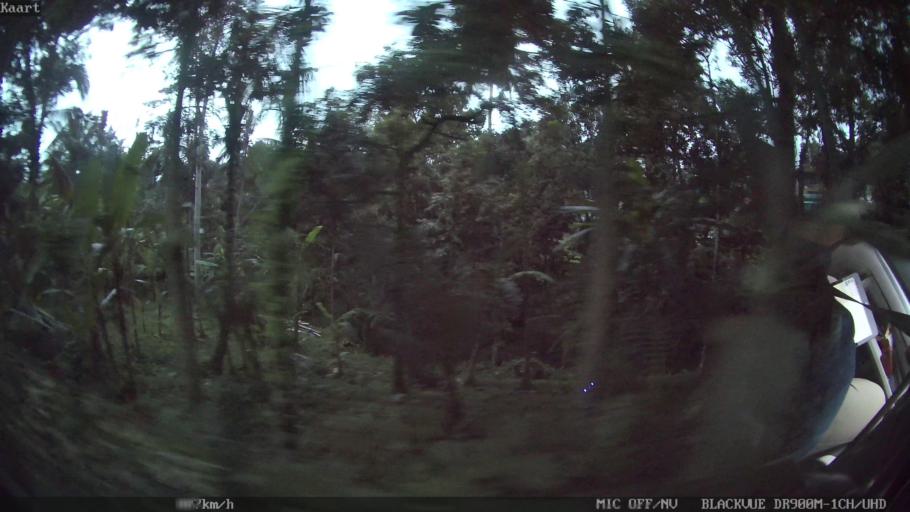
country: ID
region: Bali
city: Bayad
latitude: -8.4446
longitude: 115.2429
